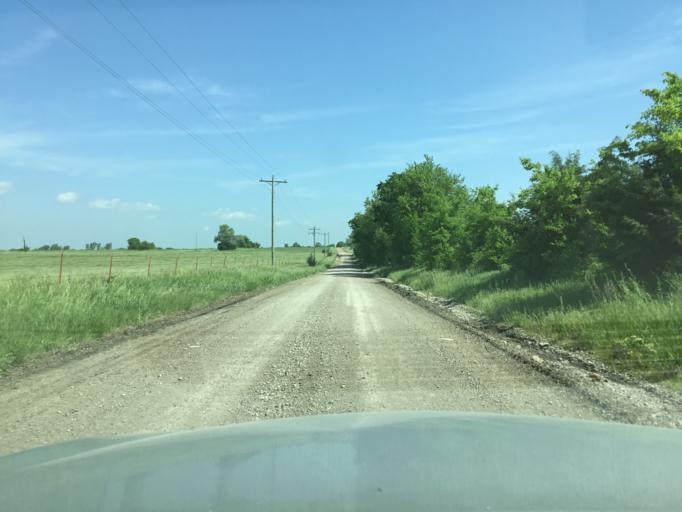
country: US
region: Kansas
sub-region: Labette County
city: Oswego
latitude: 37.1760
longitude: -95.1399
